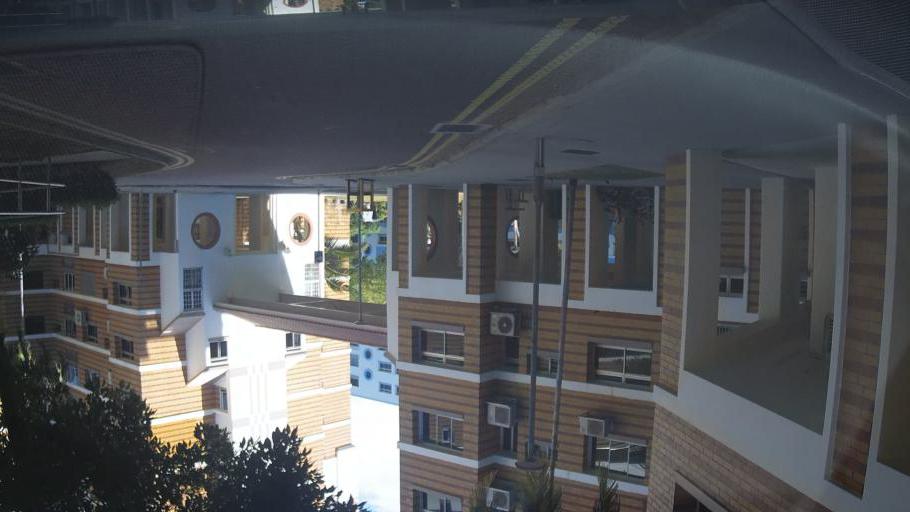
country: SG
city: Singapore
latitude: 1.3637
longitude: 103.9627
